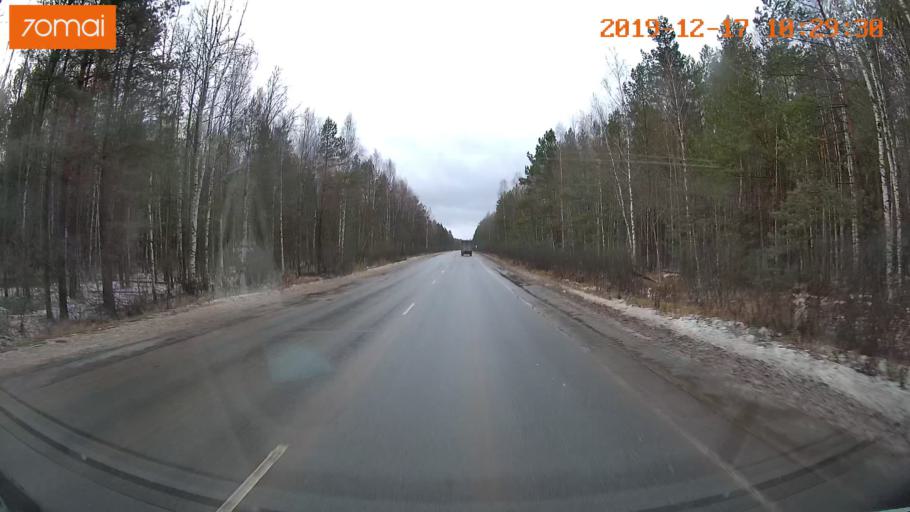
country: RU
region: Vladimir
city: Anopino
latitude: 55.6515
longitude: 40.7198
